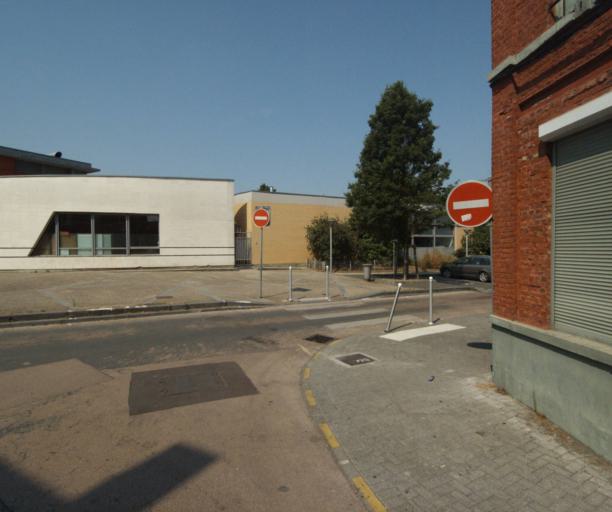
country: FR
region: Nord-Pas-de-Calais
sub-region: Departement du Nord
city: Tourcoing
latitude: 50.7291
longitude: 3.1544
